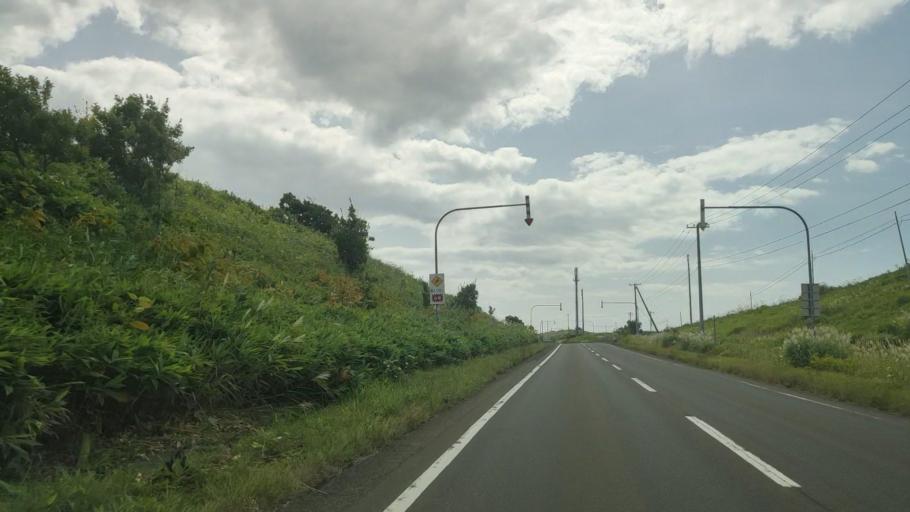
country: JP
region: Hokkaido
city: Rumoi
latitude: 44.6028
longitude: 141.7933
